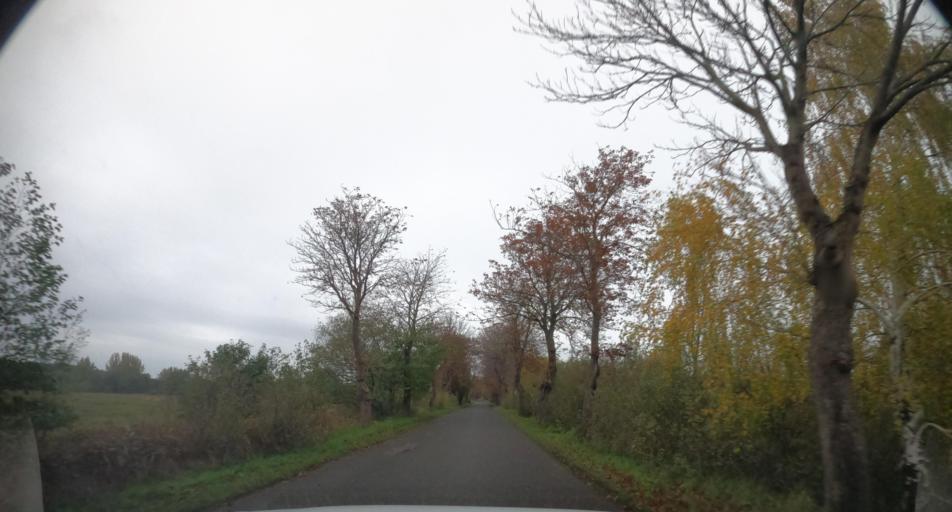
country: PL
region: West Pomeranian Voivodeship
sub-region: Powiat kamienski
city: Wolin
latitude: 53.9308
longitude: 14.6085
